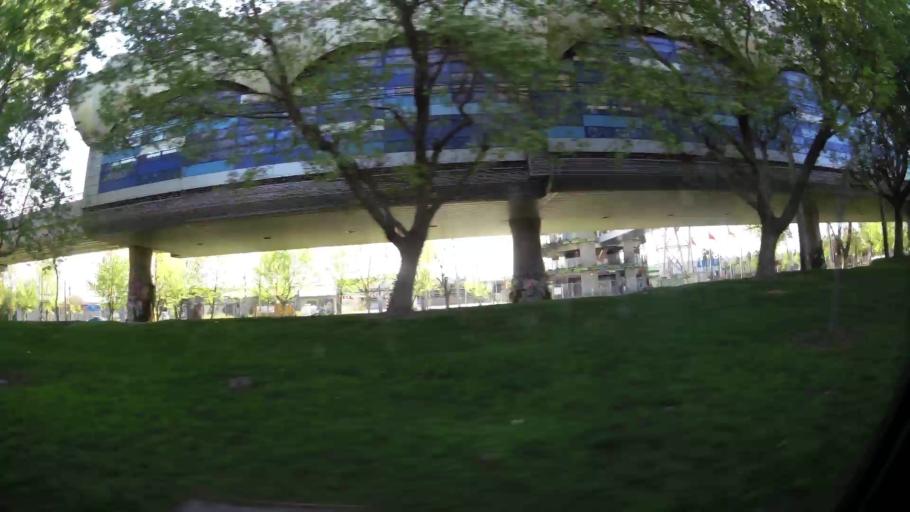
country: CL
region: Santiago Metropolitan
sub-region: Provincia de Santiago
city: Lo Prado
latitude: -33.4826
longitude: -70.7453
